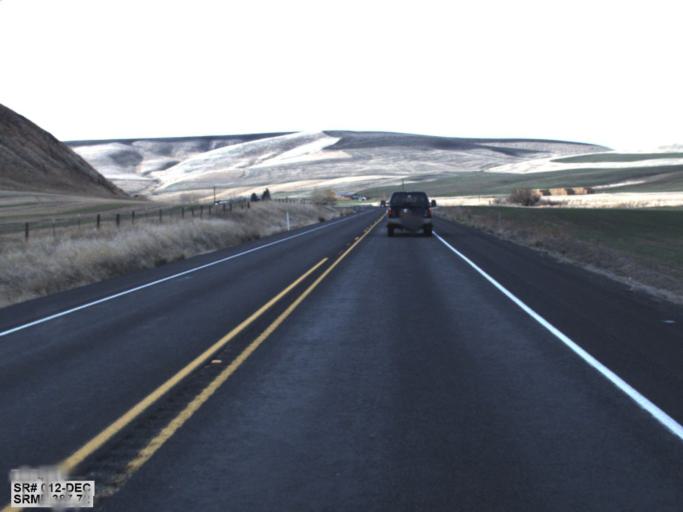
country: US
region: Washington
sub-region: Columbia County
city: Dayton
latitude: 46.5460
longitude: -117.8770
